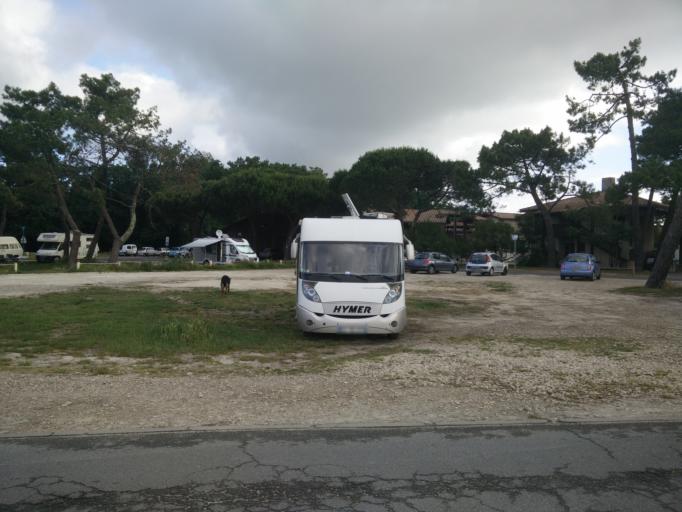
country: FR
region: Aquitaine
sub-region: Departement de la Gironde
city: Andernos-les-Bains
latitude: 44.7443
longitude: -1.1095
